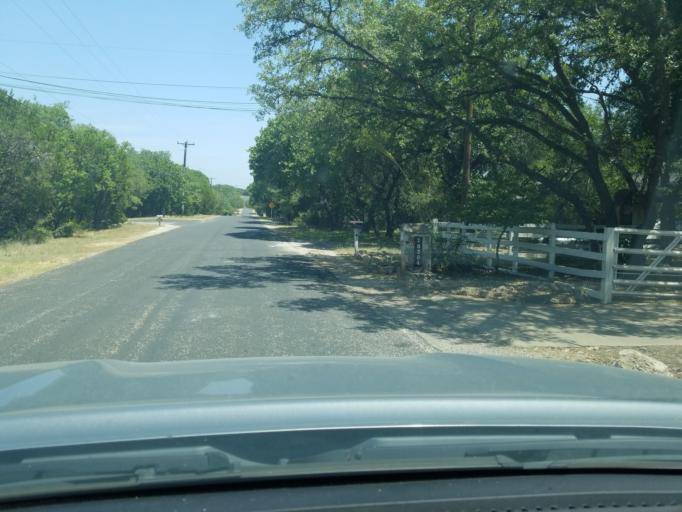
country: US
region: Texas
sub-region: Bexar County
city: Timberwood Park
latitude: 29.7166
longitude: -98.4924
